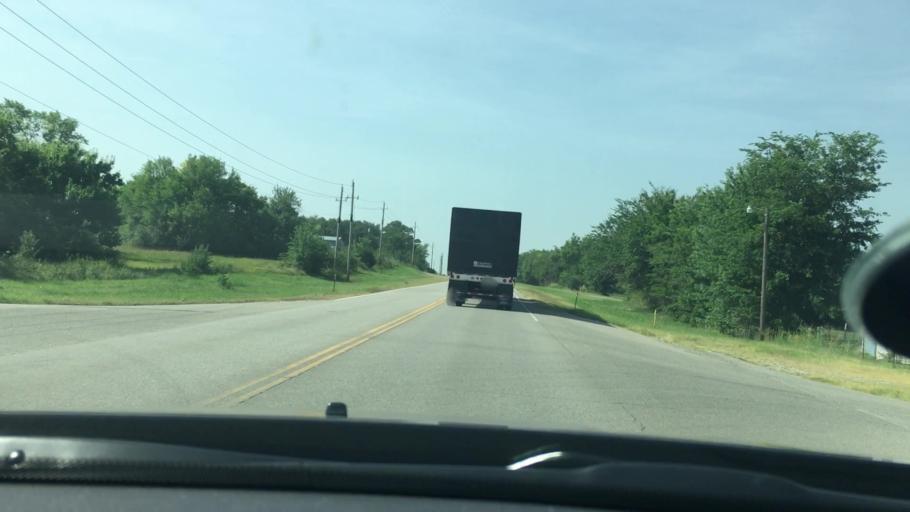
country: US
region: Oklahoma
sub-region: Coal County
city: Coalgate
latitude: 34.4692
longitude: -96.2175
